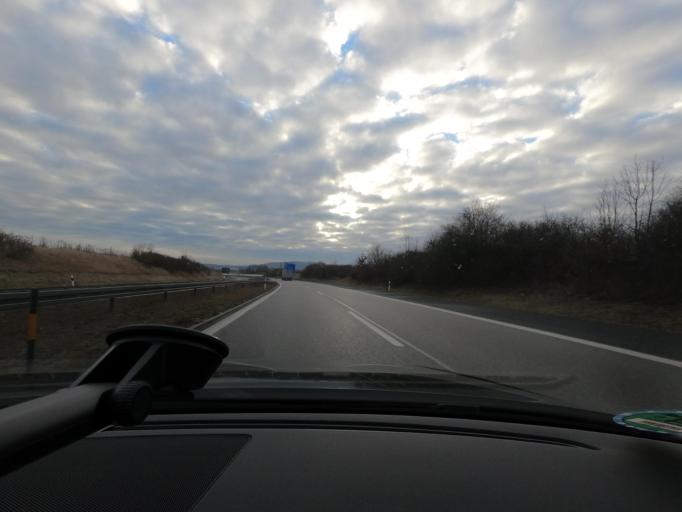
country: DE
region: Bavaria
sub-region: Upper Franconia
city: Coburg
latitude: 50.2938
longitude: 10.9663
